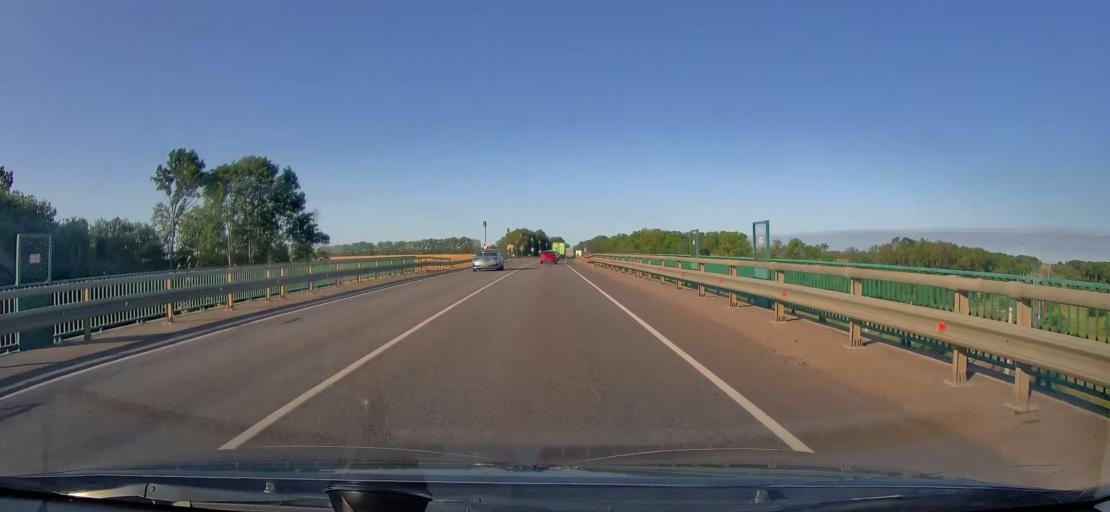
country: RU
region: Tula
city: Plavsk
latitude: 53.6038
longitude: 37.1720
